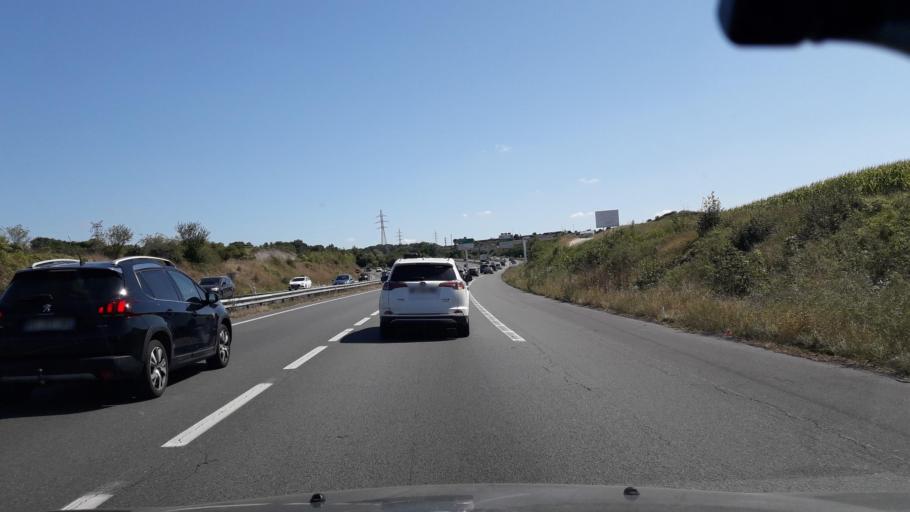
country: FR
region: Poitou-Charentes
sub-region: Departement de la Charente
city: Gond-Pontouvre
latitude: 45.6923
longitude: 0.1662
